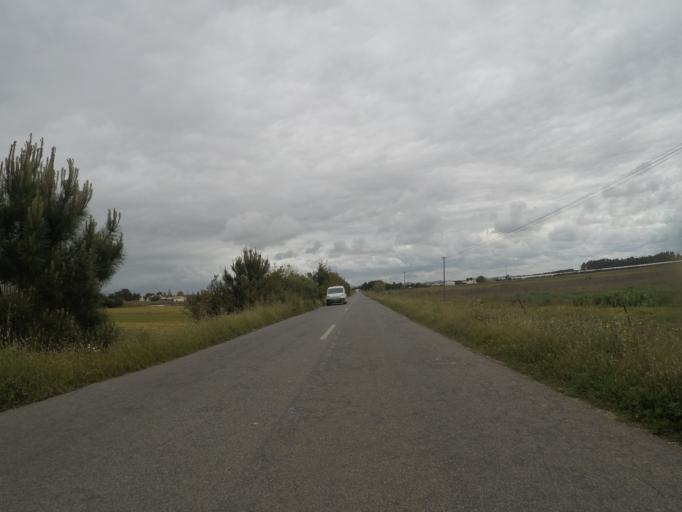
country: PT
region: Beja
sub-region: Odemira
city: Vila Nova de Milfontes
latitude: 37.6095
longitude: -8.7954
